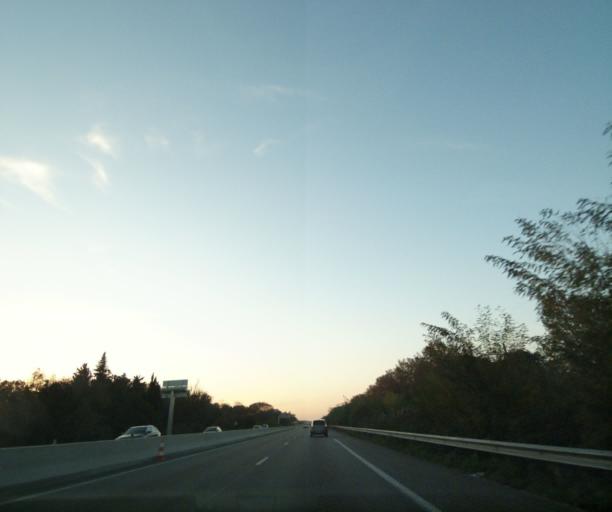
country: FR
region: Provence-Alpes-Cote d'Azur
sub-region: Departement des Bouches-du-Rhone
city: Saint-Martin-de-Crau
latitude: 43.6394
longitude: 4.7247
